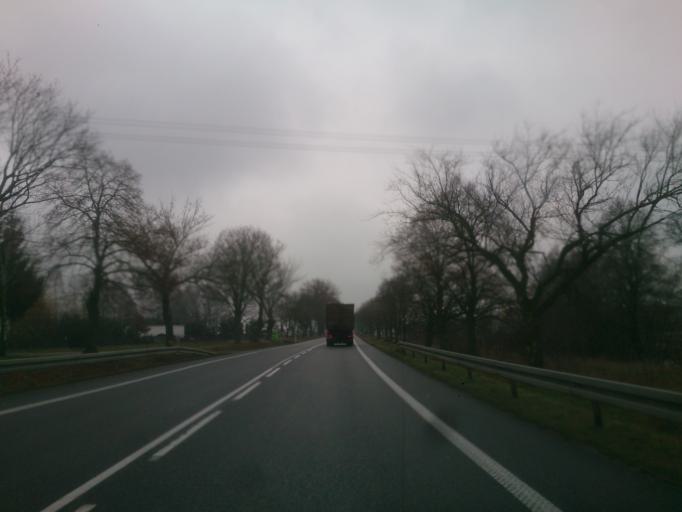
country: PL
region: Masovian Voivodeship
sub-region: Powiat sierpecki
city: Sierpc
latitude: 52.8497
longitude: 19.7067
